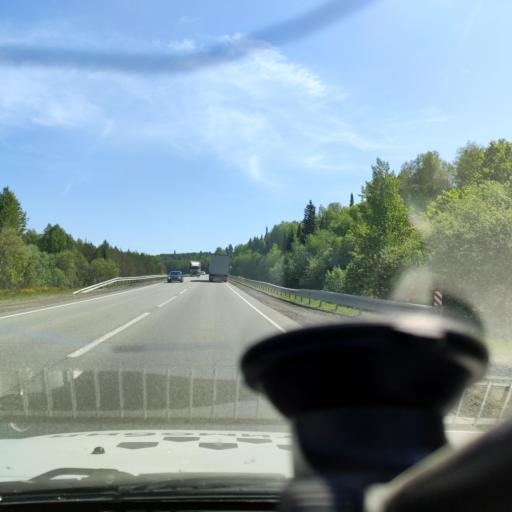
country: RU
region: Sverdlovsk
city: Ufimskiy
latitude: 56.7819
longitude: 58.2916
